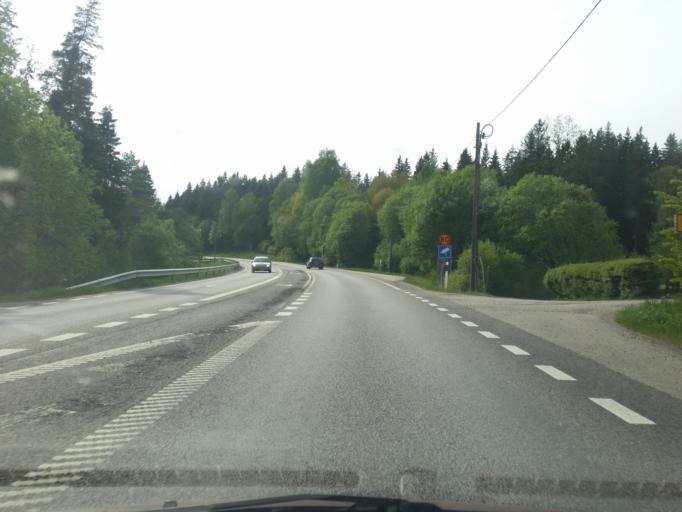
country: SE
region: Vaestra Goetaland
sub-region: Ulricehamns Kommun
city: Ulricehamn
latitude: 57.8052
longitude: 13.3247
